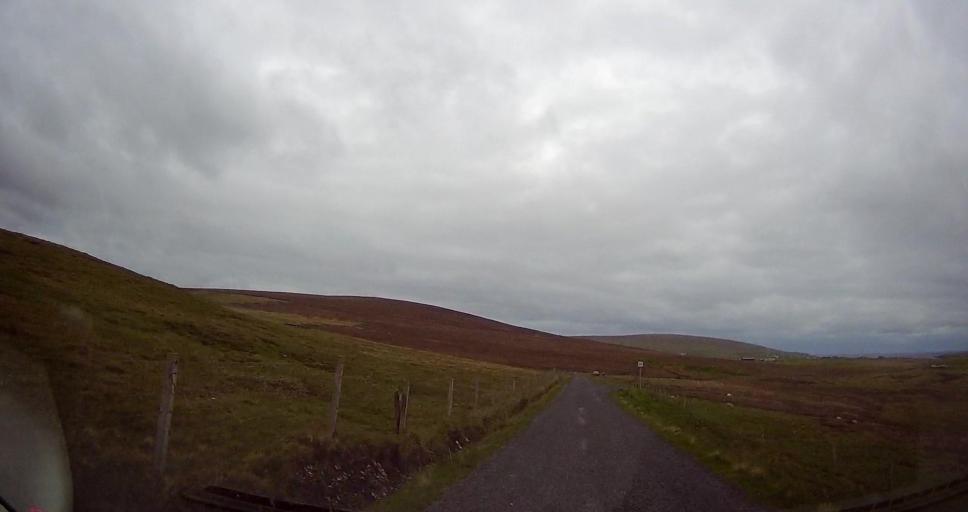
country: GB
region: Scotland
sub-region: Shetland Islands
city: Shetland
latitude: 60.7986
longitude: -0.8664
